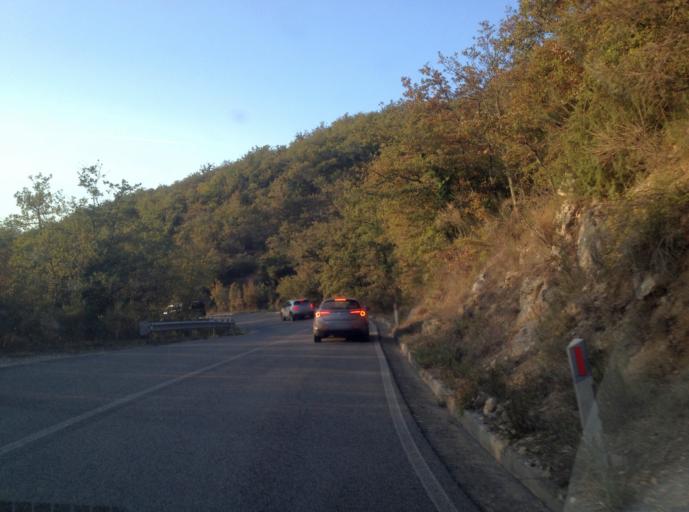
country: IT
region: Tuscany
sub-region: Provincia di Siena
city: Castellina in Chianti
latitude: 43.5027
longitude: 11.2990
